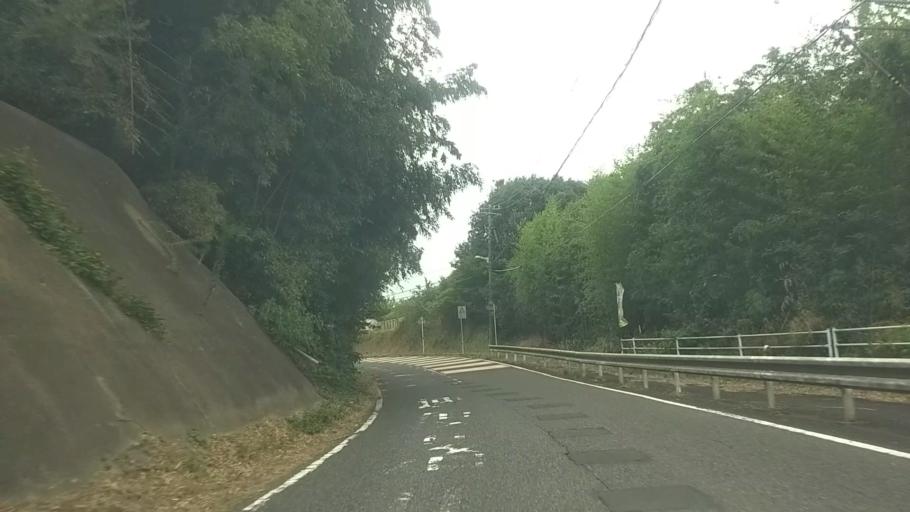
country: JP
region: Chiba
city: Kimitsu
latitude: 35.2372
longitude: 140.0008
